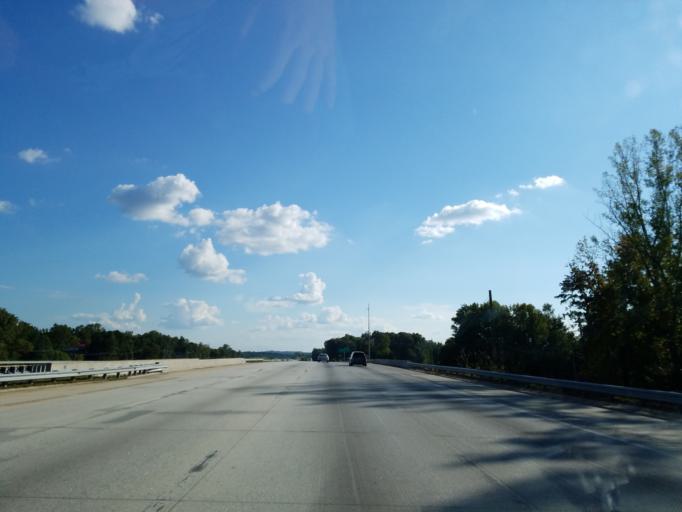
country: US
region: North Carolina
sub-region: Rowan County
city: Spencer
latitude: 35.7091
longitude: -80.3964
